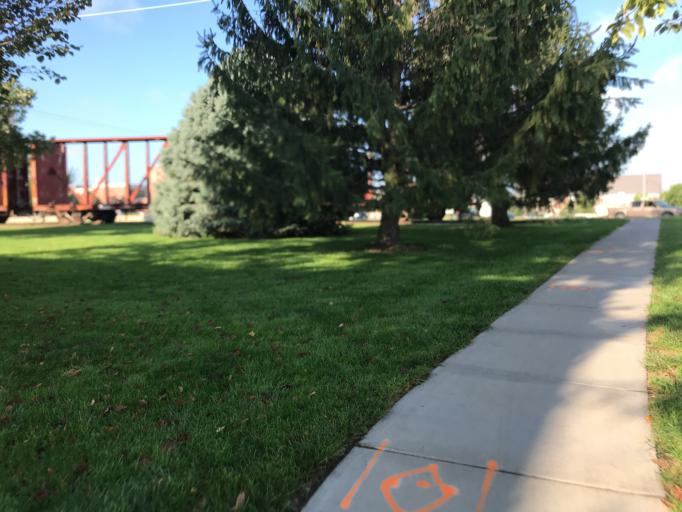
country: US
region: Nebraska
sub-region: Lancaster County
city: Lincoln
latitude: 40.8244
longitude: -96.6947
